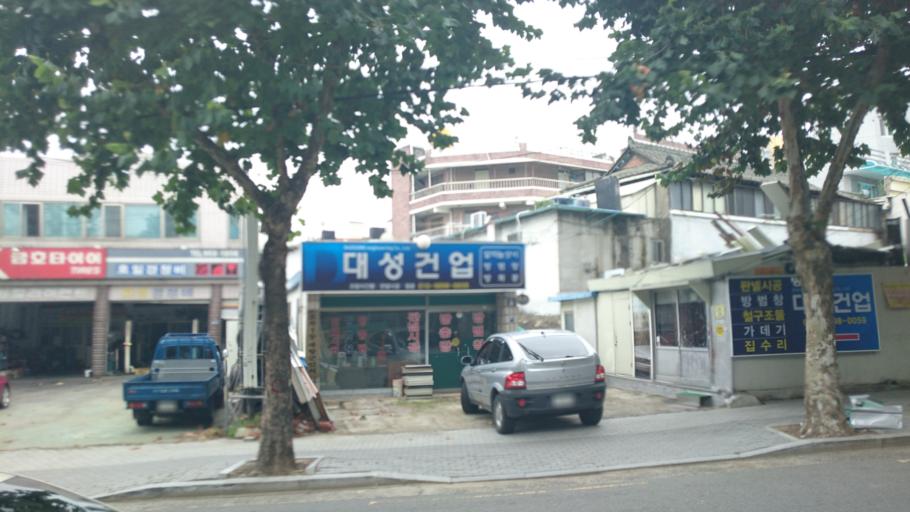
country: KR
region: Daegu
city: Daegu
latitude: 35.8808
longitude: 128.6477
